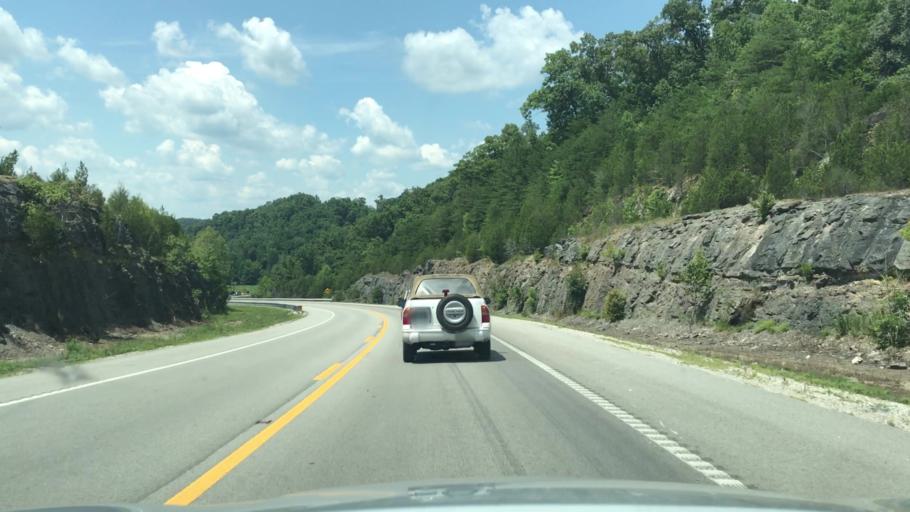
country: US
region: Tennessee
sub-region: Pickett County
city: Byrdstown
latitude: 36.6072
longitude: -85.1162
